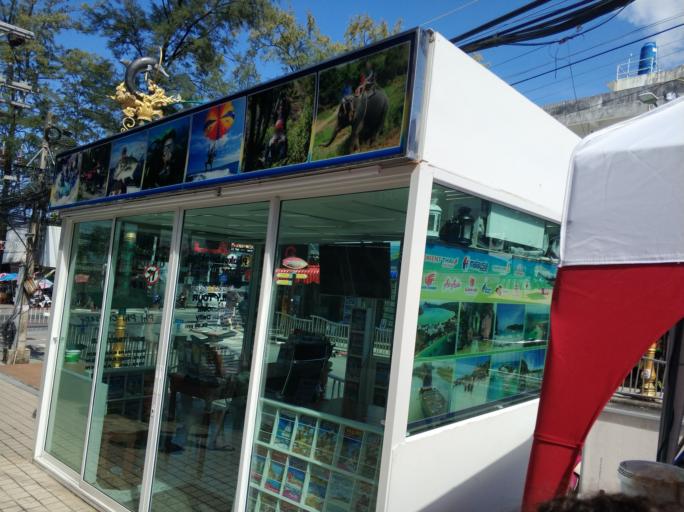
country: TH
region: Phuket
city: Patong
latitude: 7.8976
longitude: 98.2969
